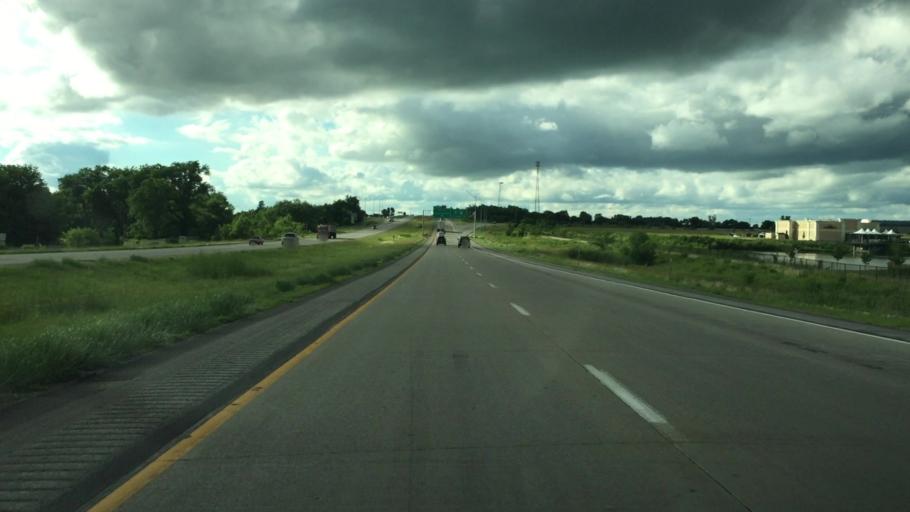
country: US
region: Iowa
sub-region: Polk County
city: Altoona
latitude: 41.6522
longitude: -93.5159
